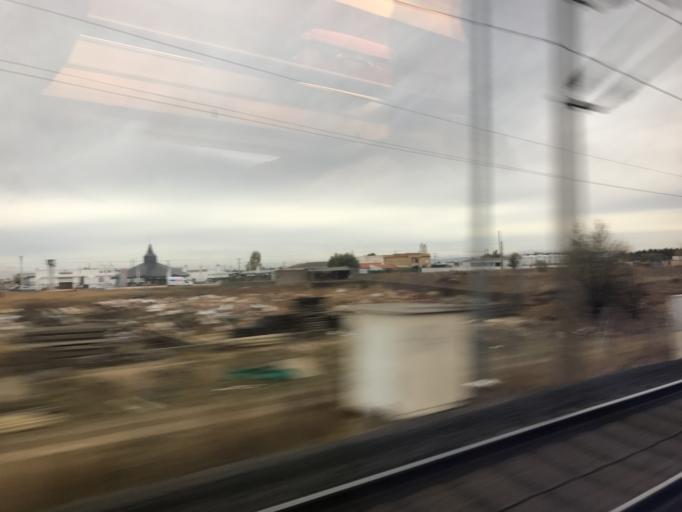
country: ES
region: Castille-La Mancha
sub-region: Provincia de Ciudad Real
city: Ciudad Real
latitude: 39.0102
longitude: -3.9236
